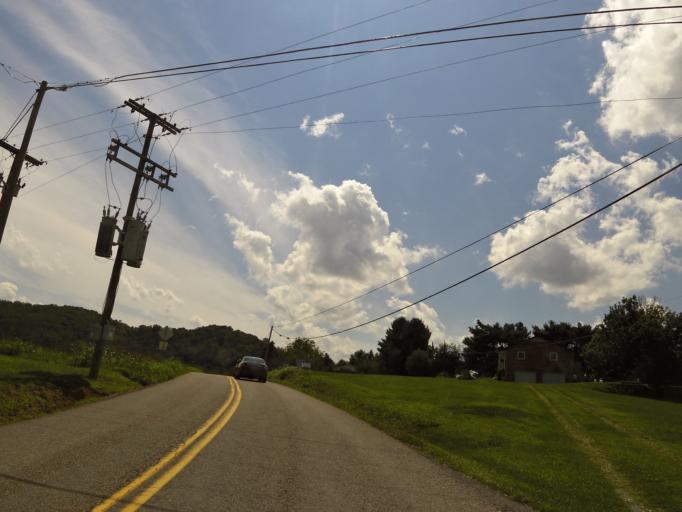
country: US
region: Virginia
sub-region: Washington County
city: Abingdon
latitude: 36.6766
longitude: -81.9392
